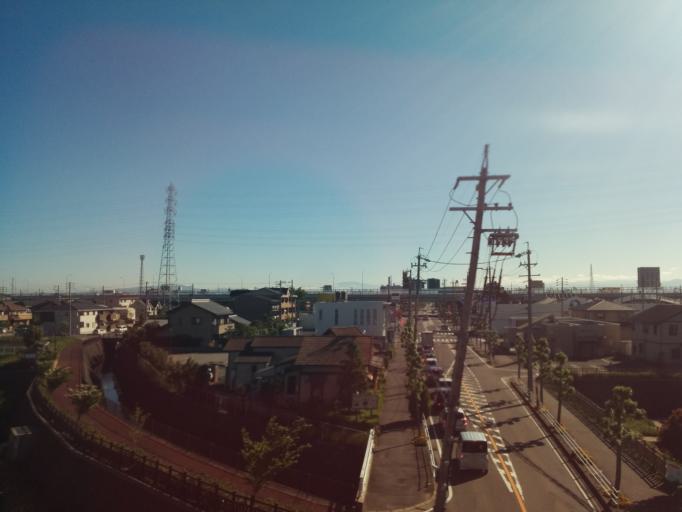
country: JP
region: Aichi
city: Chiryu
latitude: 34.9976
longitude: 137.0270
